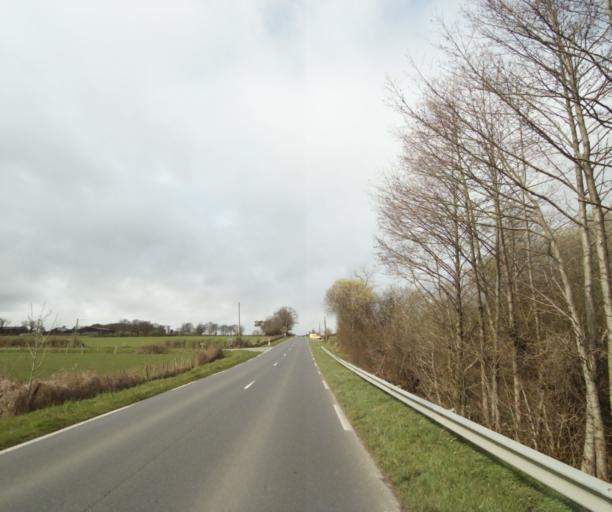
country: FR
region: Pays de la Loire
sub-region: Departement de la Loire-Atlantique
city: Bouvron
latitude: 47.4183
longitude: -1.8744
